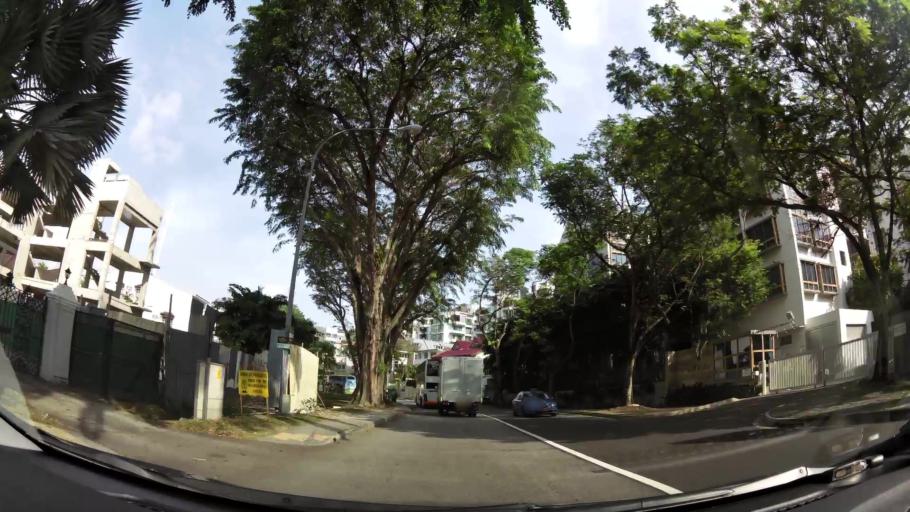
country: SG
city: Singapore
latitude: 1.2802
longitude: 103.7853
